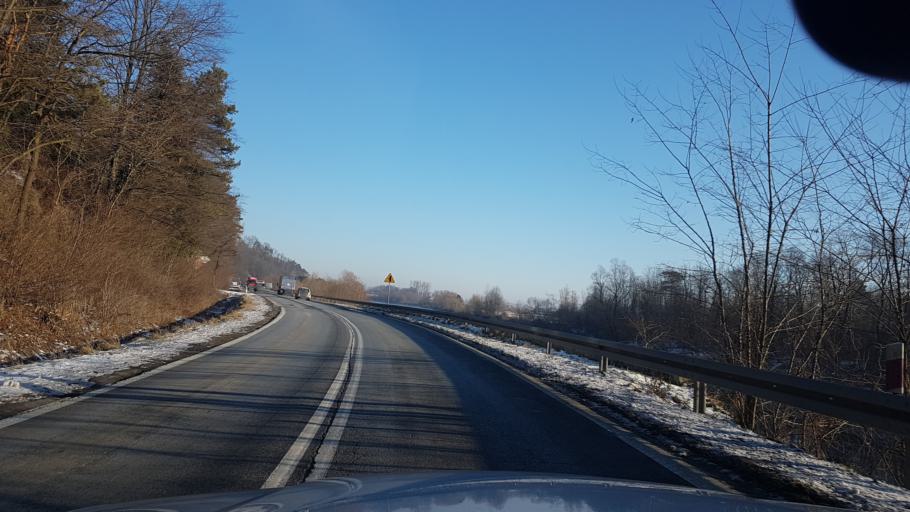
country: PL
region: Lesser Poland Voivodeship
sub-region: Powiat nowosadecki
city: Podegrodzie
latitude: 49.5427
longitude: 20.5606
